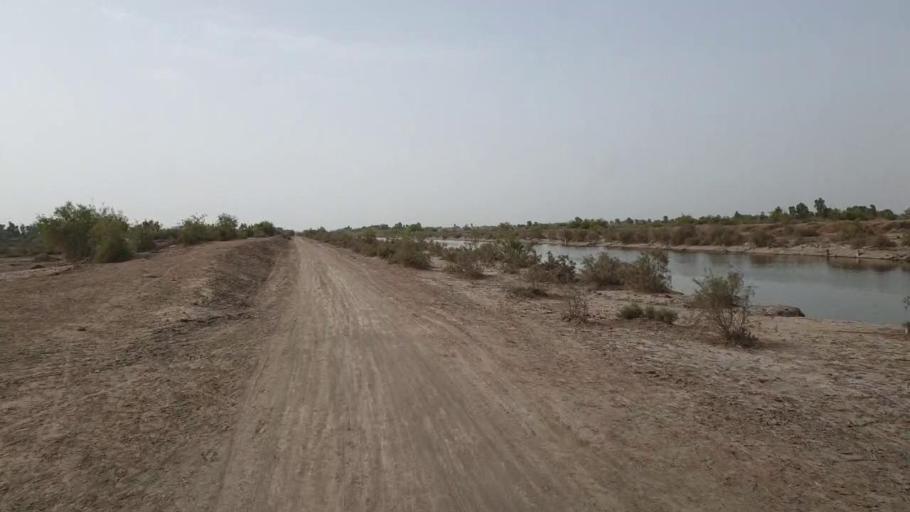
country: PK
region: Sindh
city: Daur
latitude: 26.4189
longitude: 68.1597
